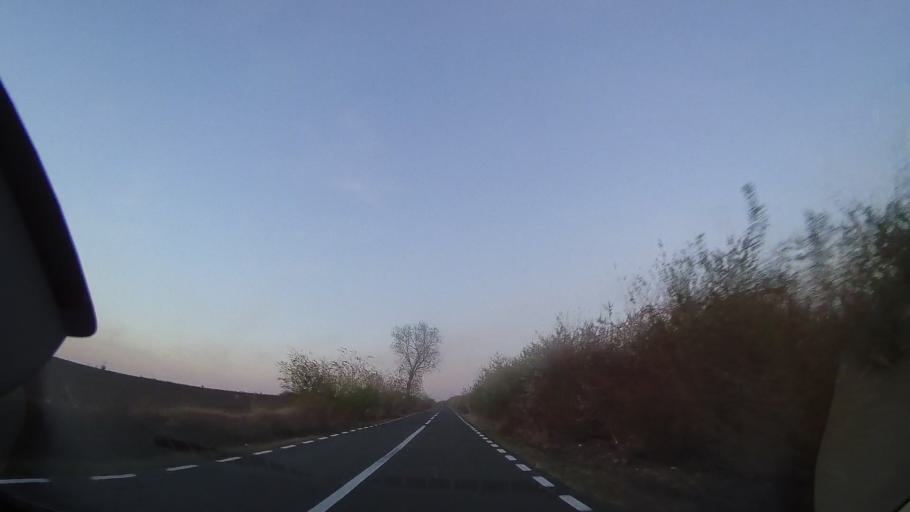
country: RO
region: Constanta
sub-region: Comuna Cobadin
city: Cobadin
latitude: 44.0314
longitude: 28.2610
